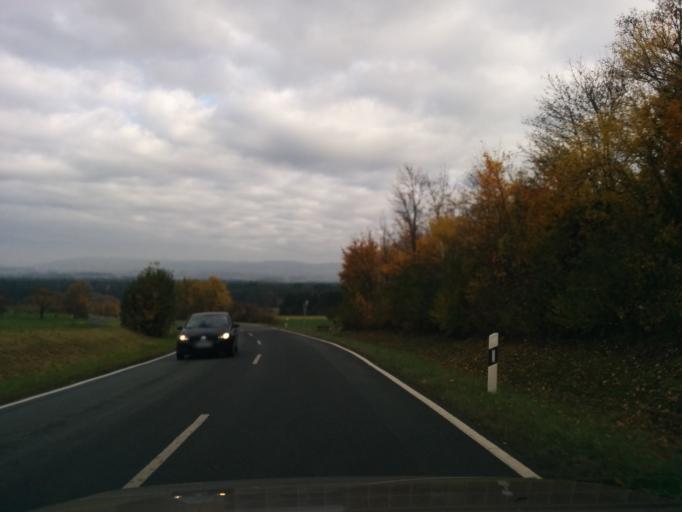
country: DE
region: Bavaria
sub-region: Regierungsbezirk Mittelfranken
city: Kalchreuth
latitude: 49.5624
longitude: 11.1244
